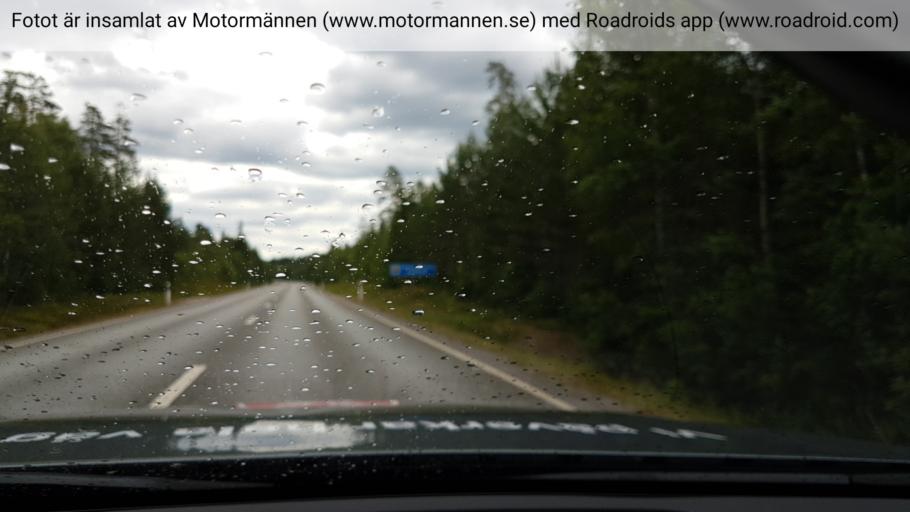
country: SE
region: Vaestmanland
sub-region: Surahammars Kommun
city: Ramnas
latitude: 59.7888
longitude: 15.9842
